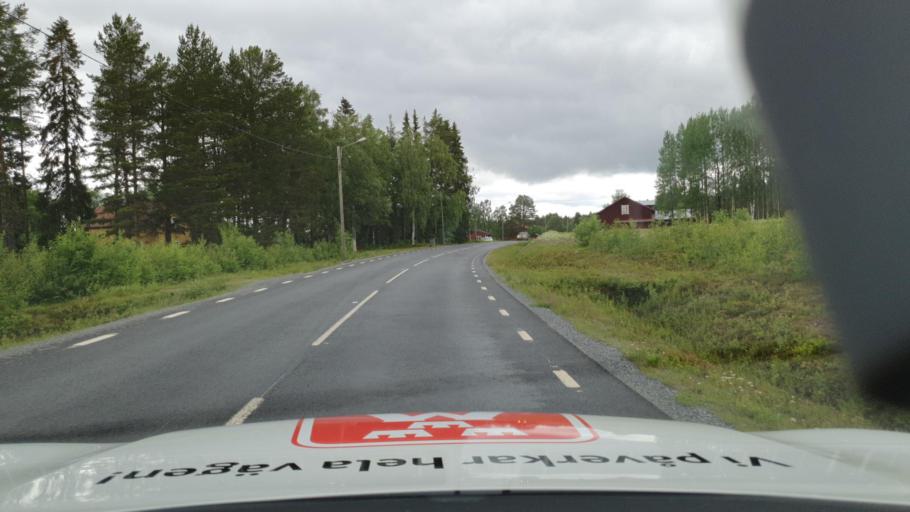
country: SE
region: Vaesterbotten
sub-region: Dorotea Kommun
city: Dorotea
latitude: 64.2187
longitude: 16.5451
